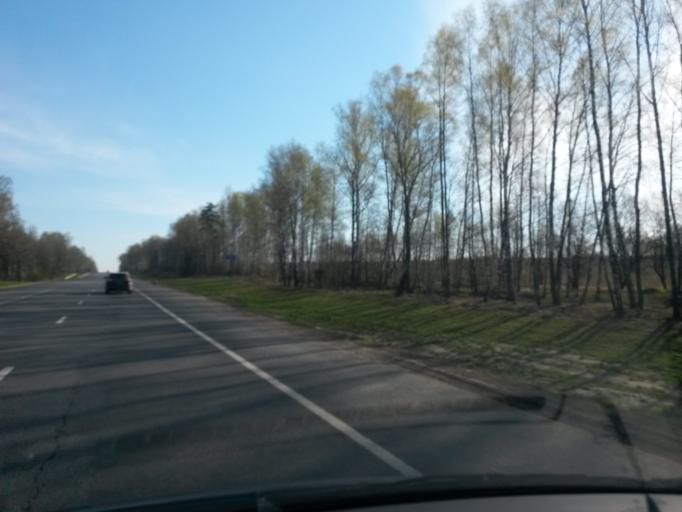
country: RU
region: Jaroslavl
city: Petrovsk
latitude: 56.9593
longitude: 39.1891
